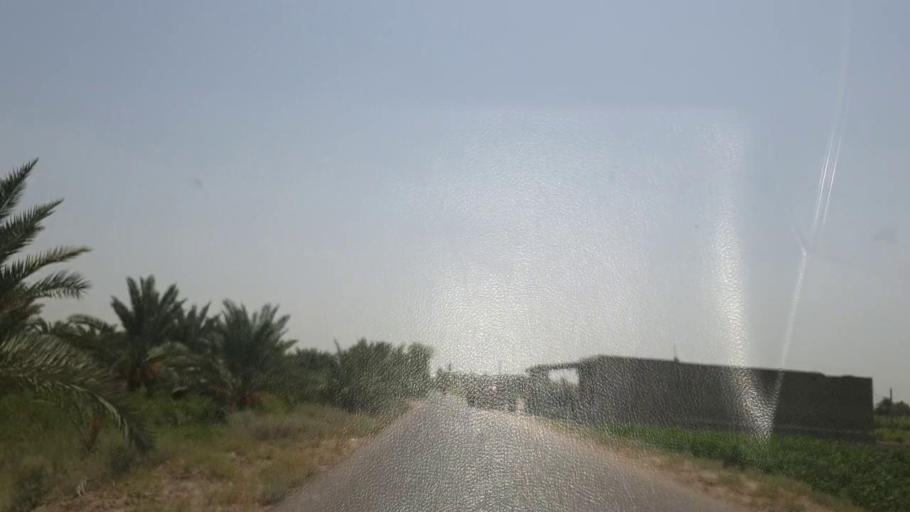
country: PK
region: Sindh
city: Kot Diji
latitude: 27.2835
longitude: 68.6268
